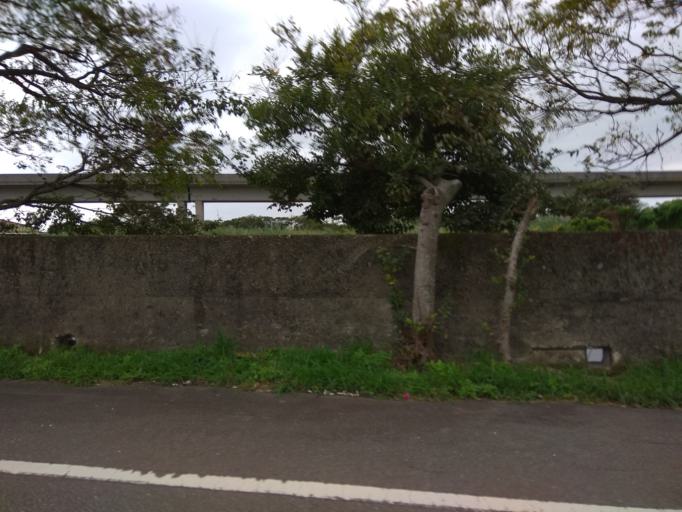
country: TW
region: Taiwan
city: Taoyuan City
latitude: 25.0485
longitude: 121.2142
